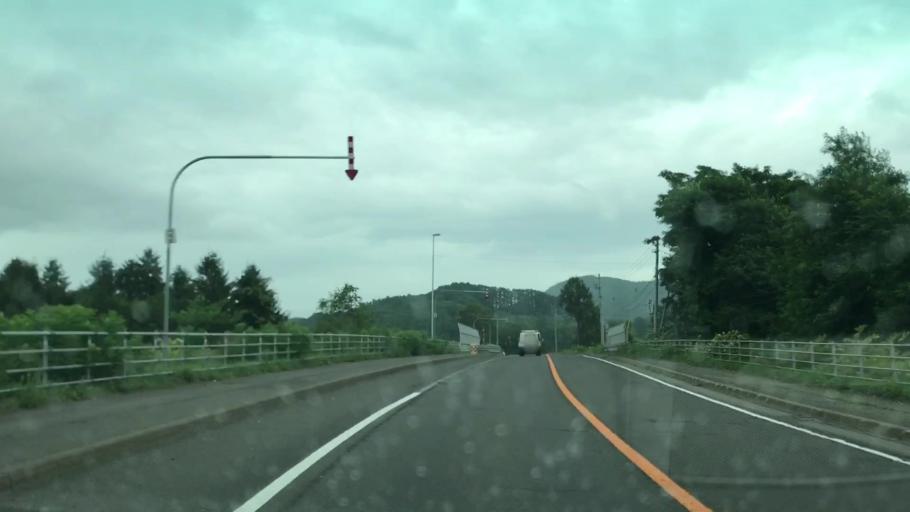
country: JP
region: Hokkaido
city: Niseko Town
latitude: 42.8101
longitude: 140.5371
